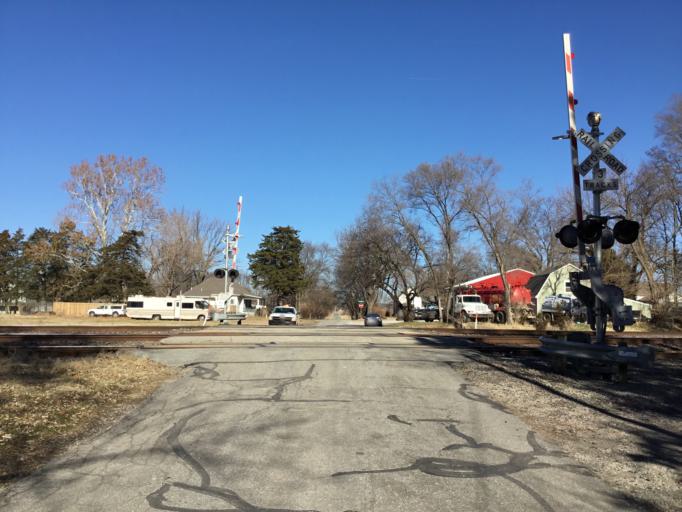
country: US
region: Kansas
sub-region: Douglas County
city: Lawrence
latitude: 38.9796
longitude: -95.2191
